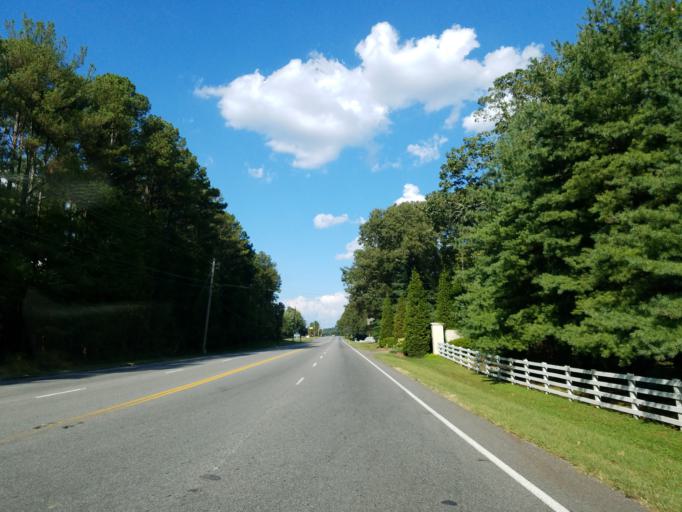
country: US
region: Georgia
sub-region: Bartow County
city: Cartersville
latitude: 34.2335
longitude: -84.7814
